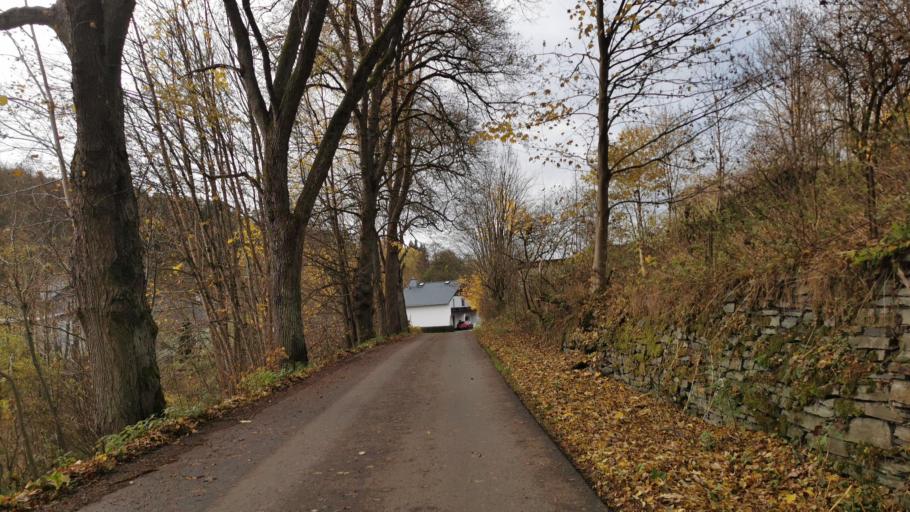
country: DE
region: Thuringia
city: Wurzbach
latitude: 50.4522
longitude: 11.5401
